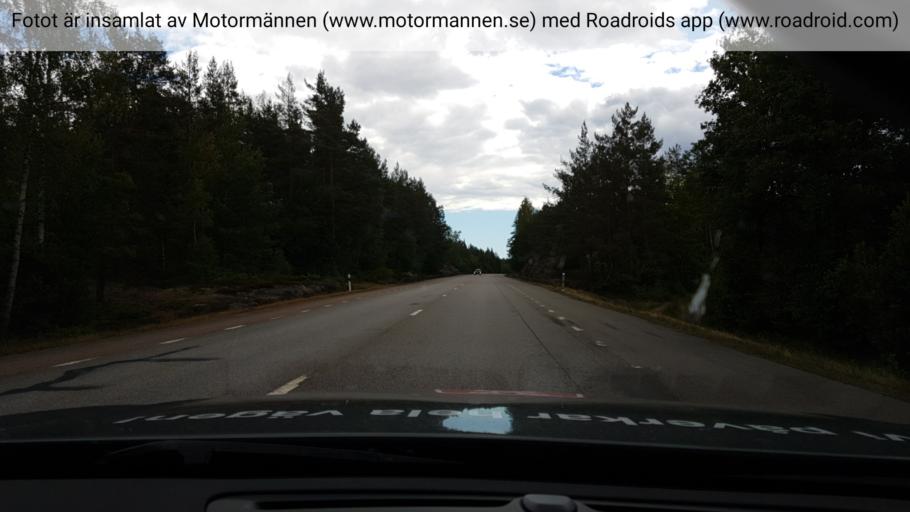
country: SE
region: Kalmar
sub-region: Vasterviks Kommun
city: Ankarsrum
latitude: 57.6378
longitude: 16.4495
